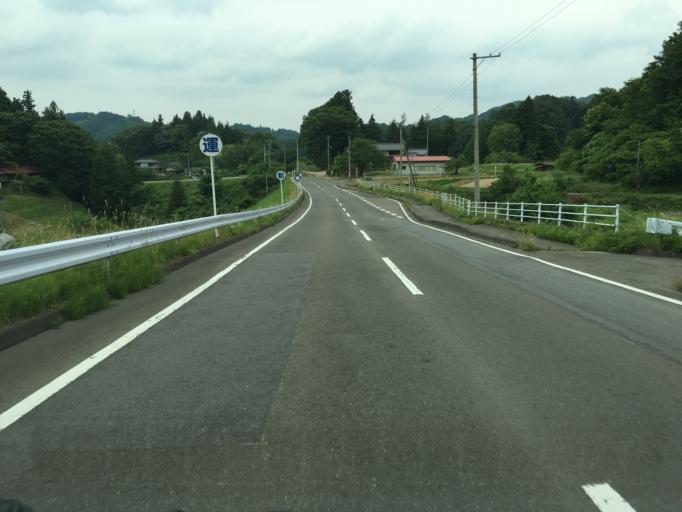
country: JP
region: Fukushima
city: Nihommatsu
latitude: 37.6116
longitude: 140.5599
